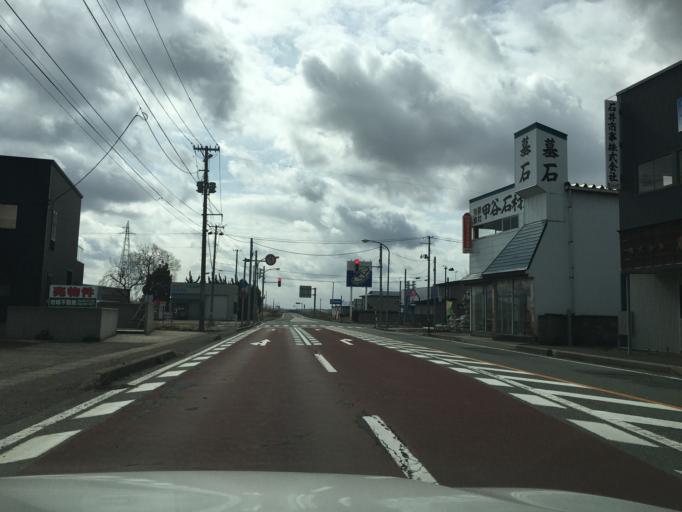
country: JP
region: Akita
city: Tenno
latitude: 39.9433
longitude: 140.0840
